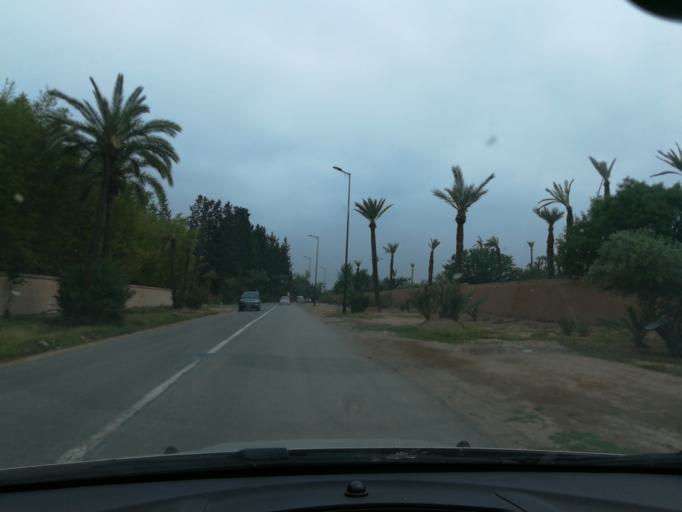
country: MA
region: Marrakech-Tensift-Al Haouz
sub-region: Marrakech
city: Marrakesh
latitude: 31.6525
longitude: -7.9745
